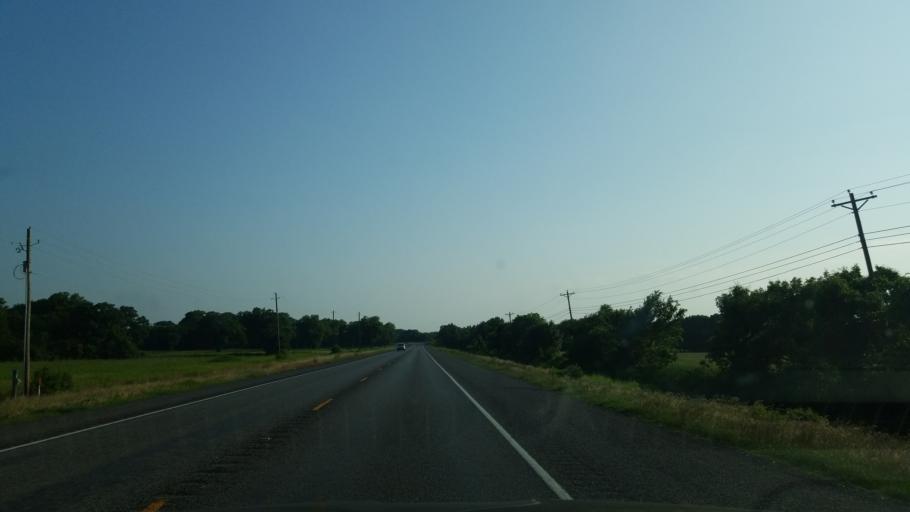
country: US
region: Texas
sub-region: Denton County
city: Denton
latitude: 33.2867
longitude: -97.0871
